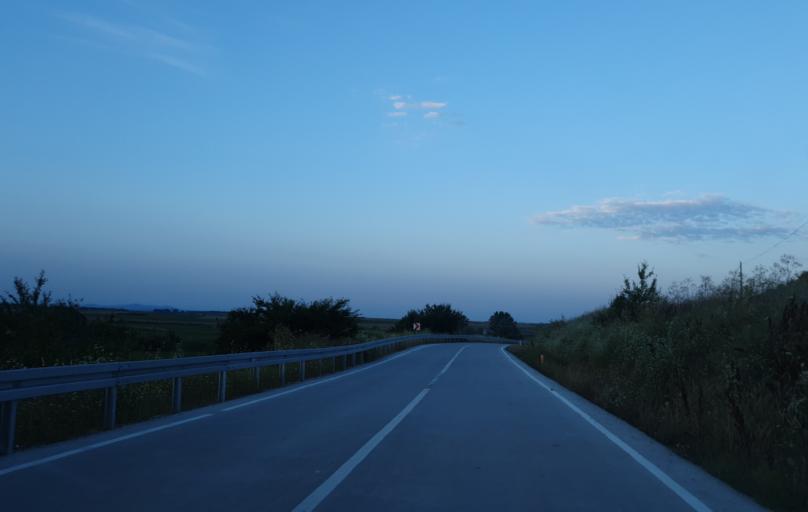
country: TR
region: Tekirdag
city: Velimese
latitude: 41.3550
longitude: 27.8504
